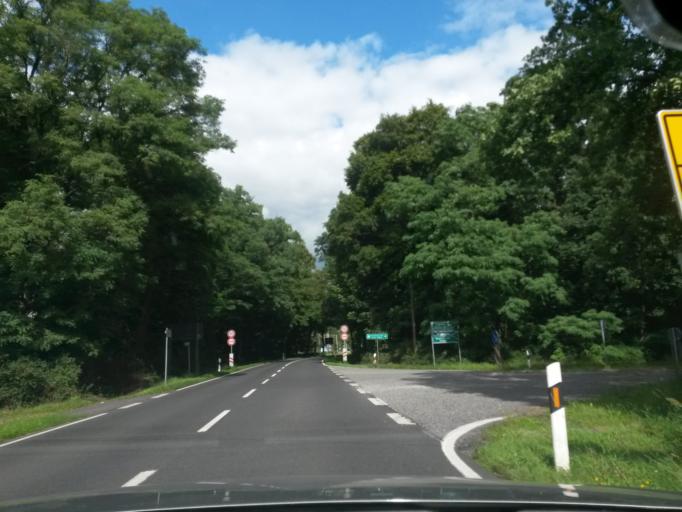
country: DE
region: Brandenburg
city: Chorin
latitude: 52.9181
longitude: 13.9037
